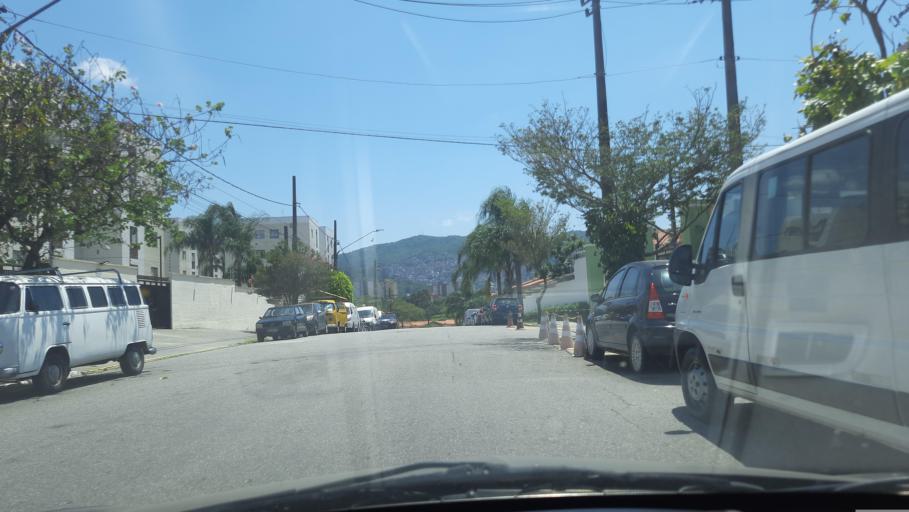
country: BR
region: Sao Paulo
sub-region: Caieiras
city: Caieiras
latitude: -23.4435
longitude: -46.7284
